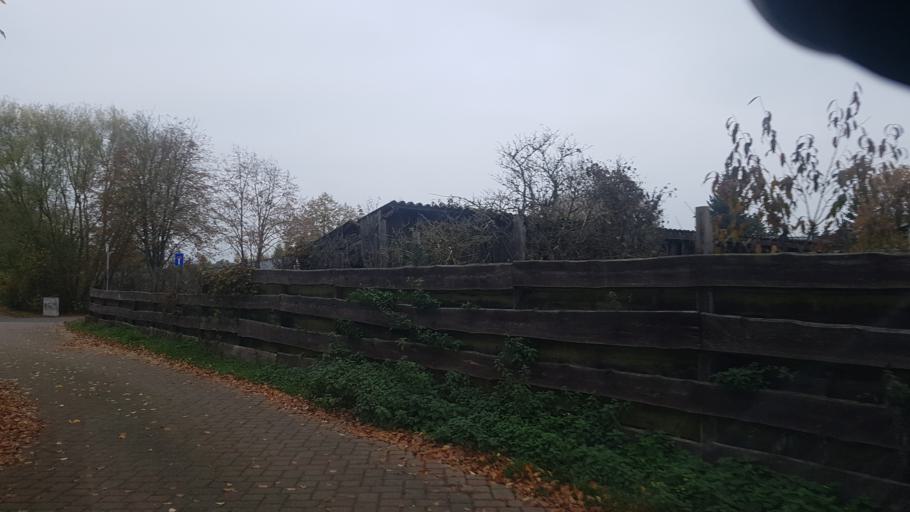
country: DE
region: Brandenburg
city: Schonermark
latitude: 52.9204
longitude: 13.1330
